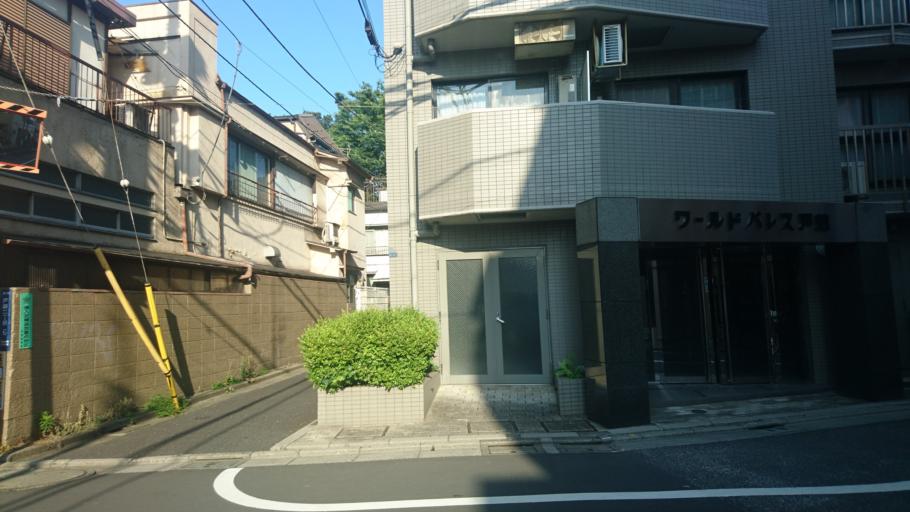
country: JP
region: Tokyo
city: Tokyo
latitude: 35.6136
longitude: 139.7193
